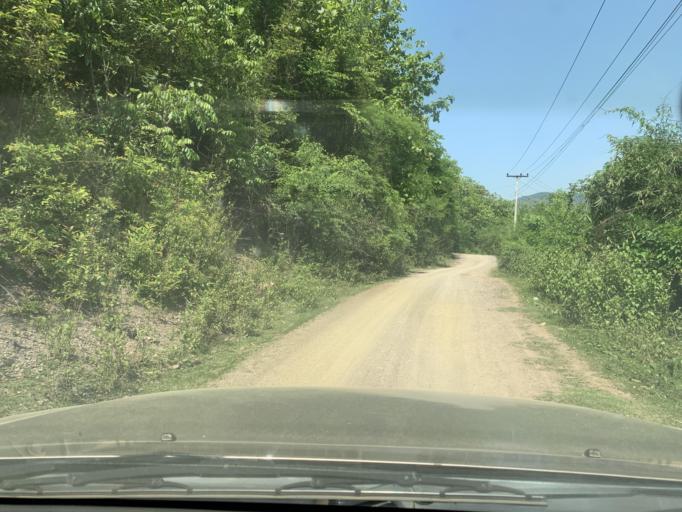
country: LA
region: Louangphabang
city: Louangphabang
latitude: 19.9134
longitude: 102.2610
